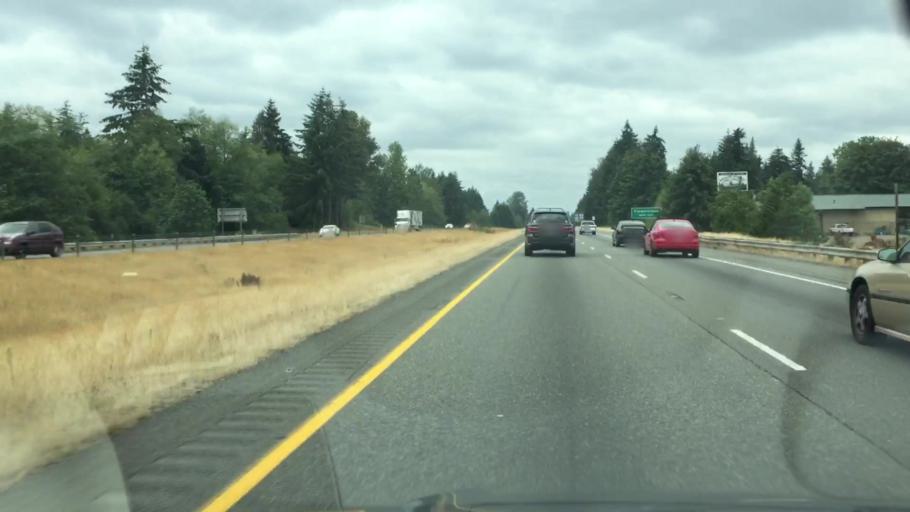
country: US
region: Washington
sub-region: Pierce County
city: Summit
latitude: 47.1580
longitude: -122.3385
